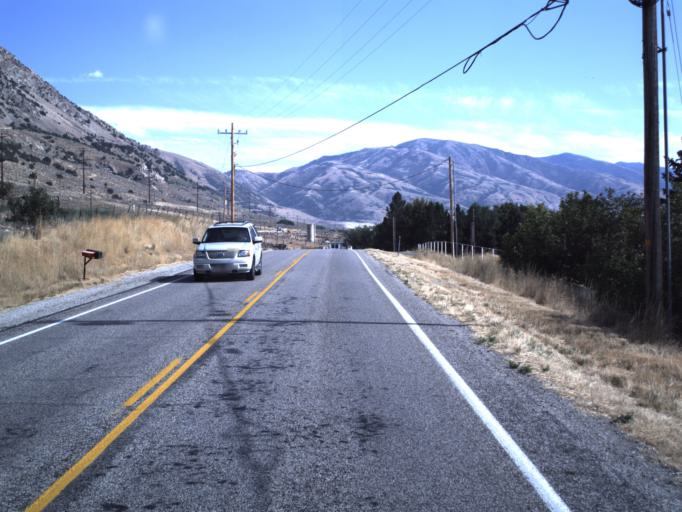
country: US
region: Utah
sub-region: Box Elder County
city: Brigham City
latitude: 41.5491
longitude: -112.0176
